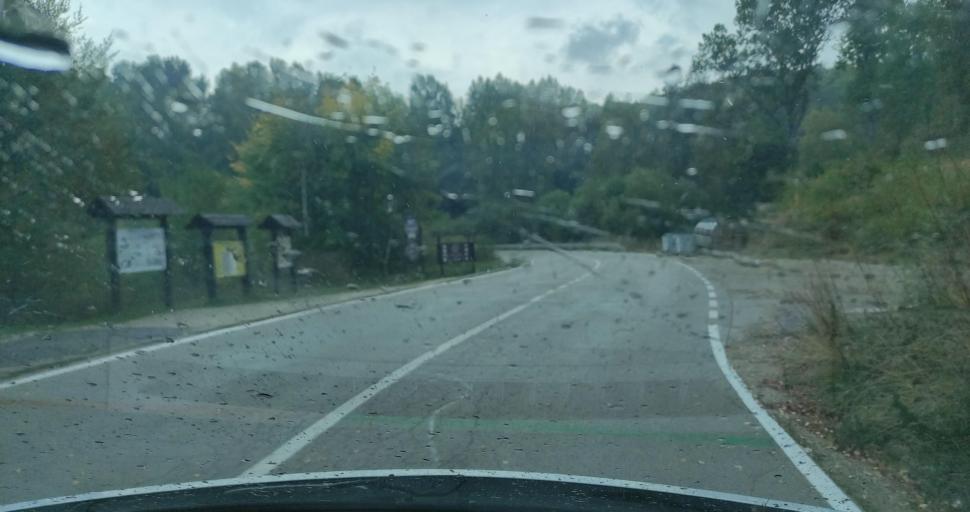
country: RS
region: Central Serbia
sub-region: Jablanicki Okrug
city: Crna Trava
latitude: 42.7390
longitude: 22.3295
